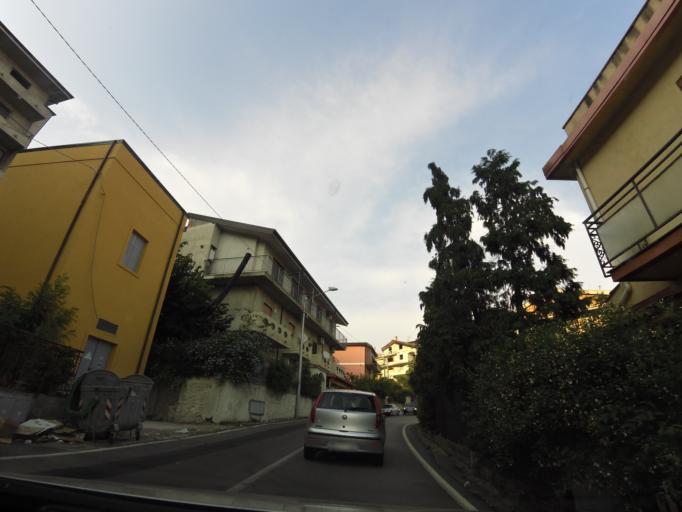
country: IT
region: Calabria
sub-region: Provincia di Reggio Calabria
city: Stilo
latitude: 38.4763
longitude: 16.4676
